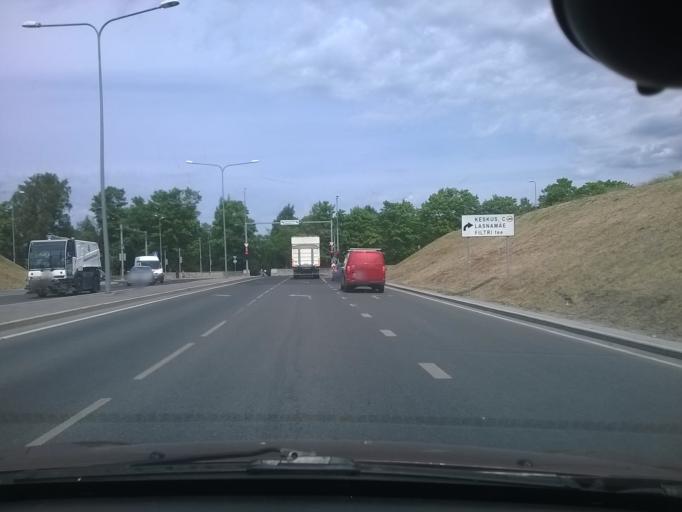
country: EE
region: Harju
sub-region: Tallinna linn
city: Tallinn
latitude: 59.4202
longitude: 24.7659
